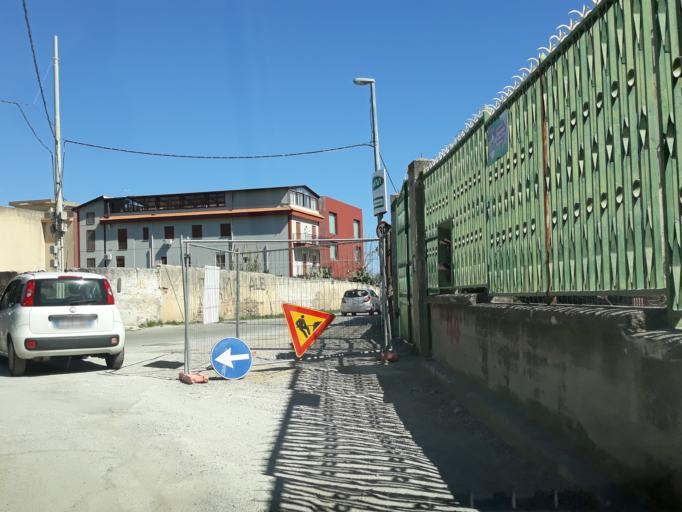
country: IT
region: Sicily
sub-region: Palermo
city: Villa Ciambra
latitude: 38.0907
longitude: 13.3210
